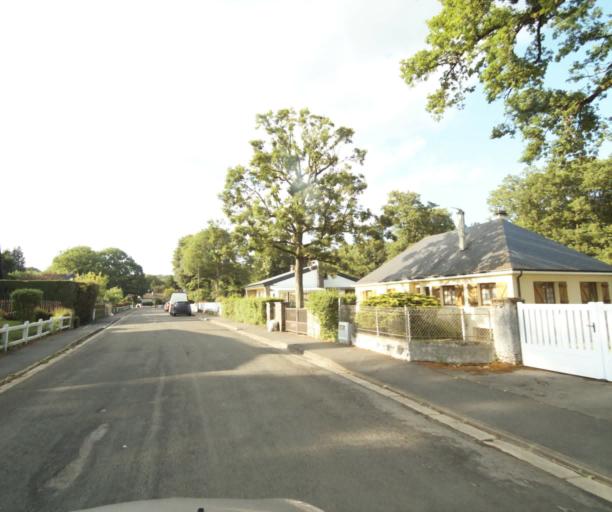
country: FR
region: Champagne-Ardenne
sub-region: Departement des Ardennes
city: Charleville-Mezieres
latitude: 49.7976
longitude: 4.7149
